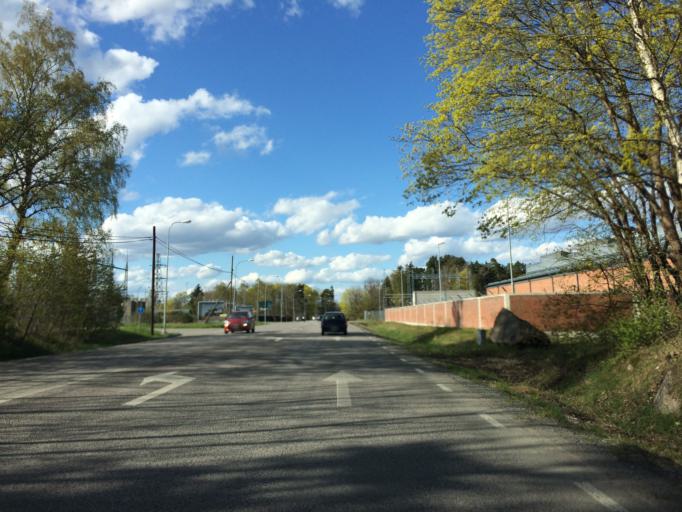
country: SE
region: Stockholm
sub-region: Sollentuna Kommun
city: Sollentuna
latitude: 59.4463
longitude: 17.9258
